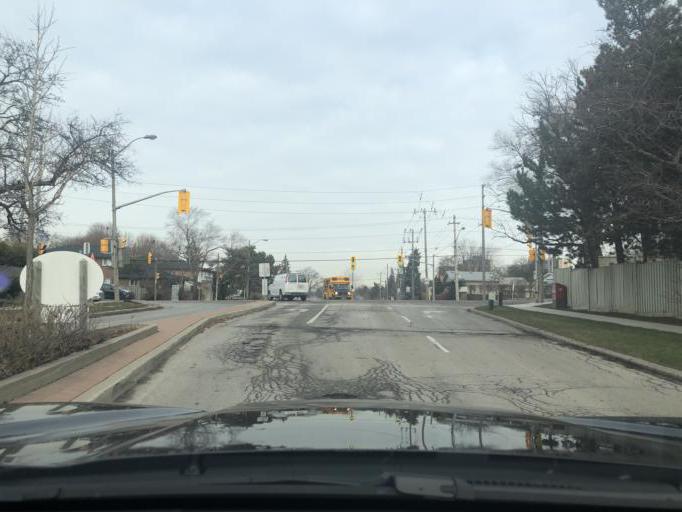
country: CA
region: Ontario
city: Willowdale
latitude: 43.7733
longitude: -79.3531
